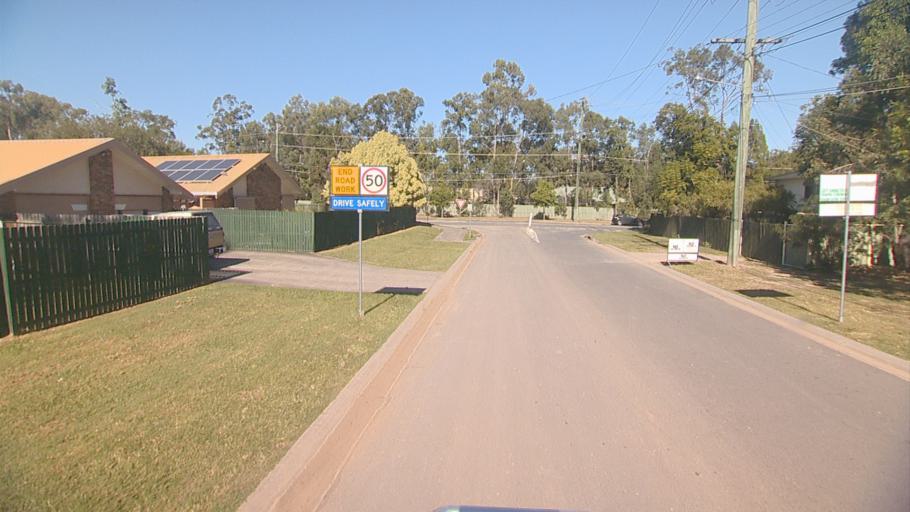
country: AU
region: Queensland
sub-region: Logan
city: Waterford West
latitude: -27.6694
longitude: 153.1316
